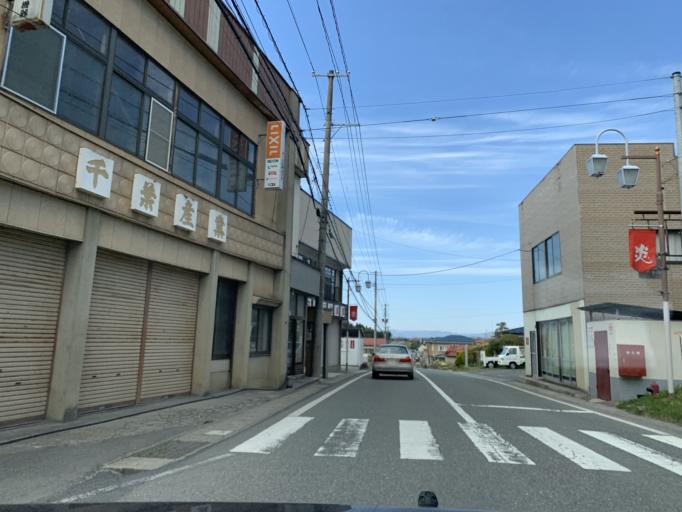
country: JP
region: Iwate
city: Ichinoseki
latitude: 38.8566
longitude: 141.3488
